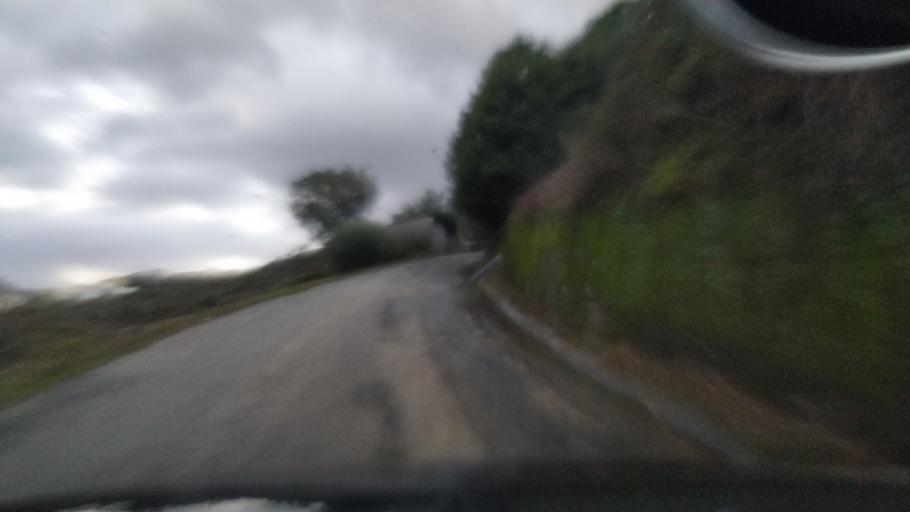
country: PT
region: Vila Real
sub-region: Santa Marta de Penaguiao
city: Santa Marta de Penaguiao
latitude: 41.2311
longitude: -7.7802
